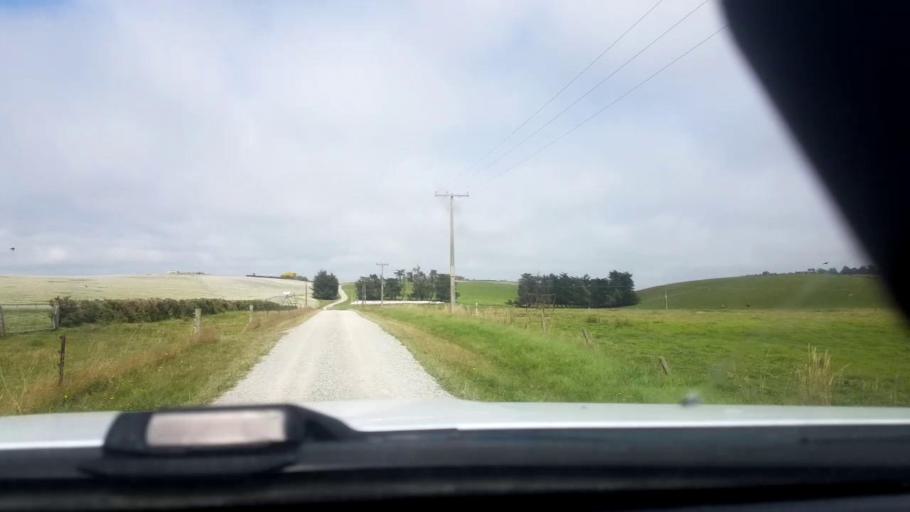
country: NZ
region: Canterbury
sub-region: Timaru District
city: Timaru
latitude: -44.3299
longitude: 171.2020
